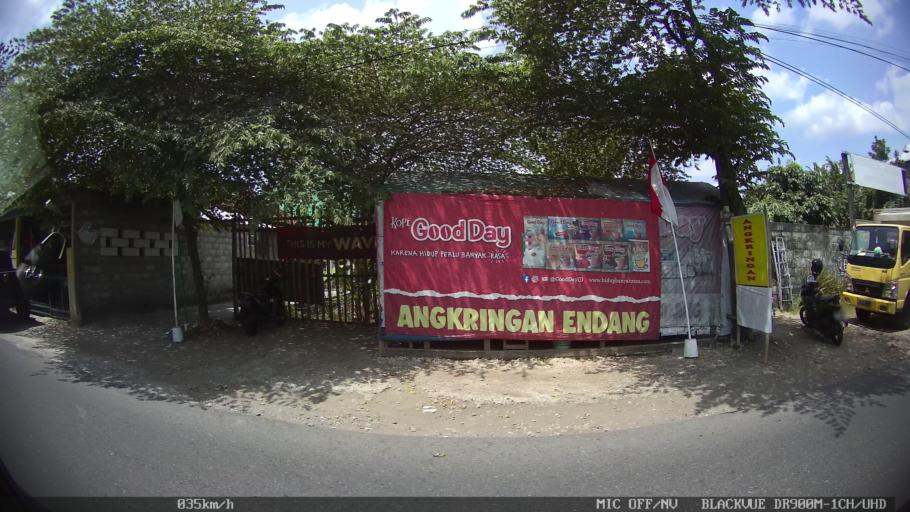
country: ID
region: Daerah Istimewa Yogyakarta
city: Gamping Lor
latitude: -7.8045
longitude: 110.3411
